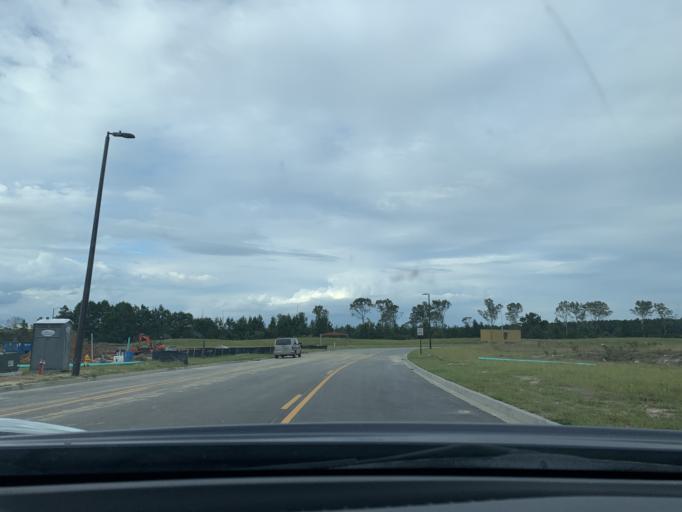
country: US
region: Georgia
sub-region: Chatham County
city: Pooler
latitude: 32.0803
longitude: -81.2801
